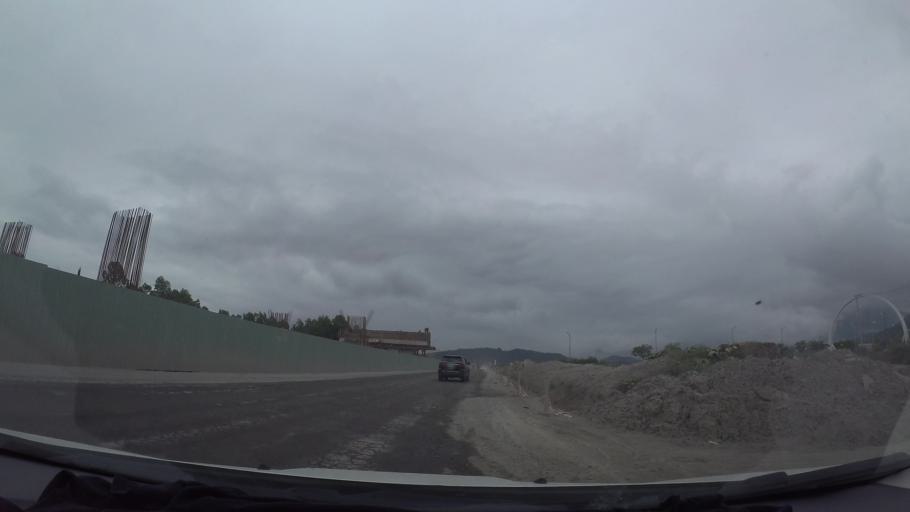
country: VN
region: Da Nang
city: Lien Chieu
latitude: 16.0939
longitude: 108.0874
